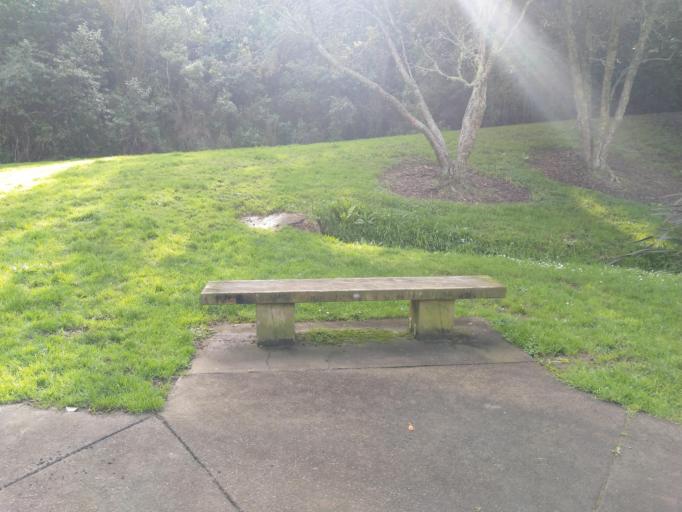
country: NZ
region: Auckland
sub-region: Auckland
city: Mangere
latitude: -36.9332
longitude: 174.7338
